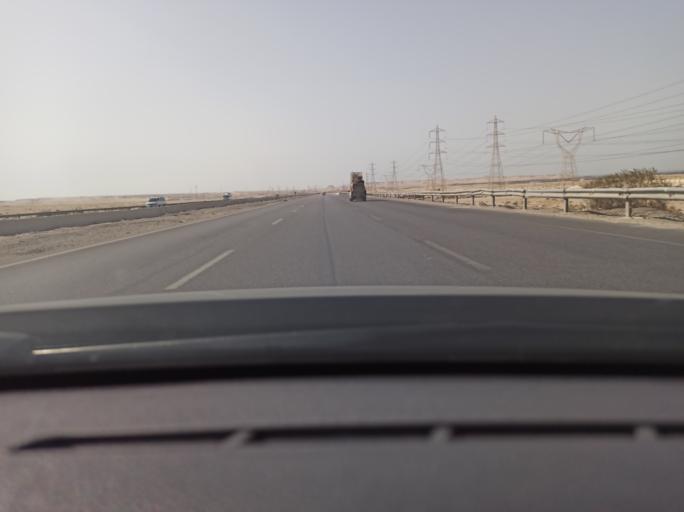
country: EG
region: Muhafazat al Qahirah
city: Halwan
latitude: 29.7357
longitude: 31.4082
